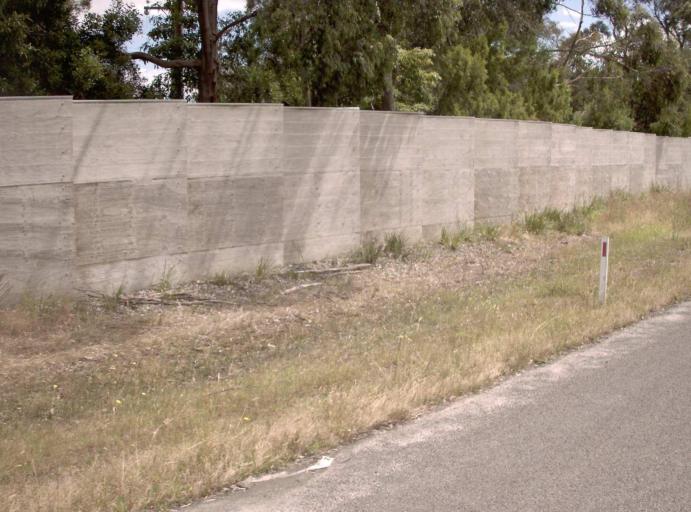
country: AU
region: Victoria
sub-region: Cardinia
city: Koo-Wee-Rup
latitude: -38.3805
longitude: 145.5543
